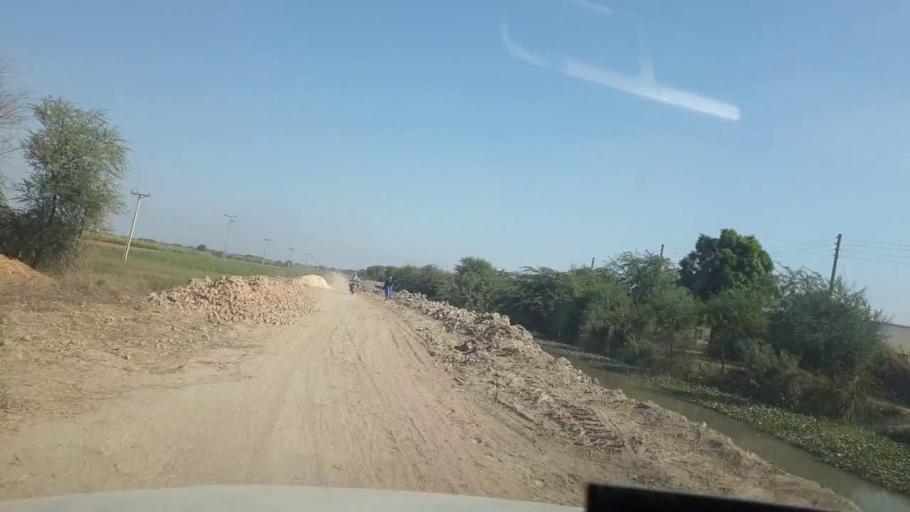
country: PK
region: Sindh
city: Kotri
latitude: 25.1596
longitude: 68.3105
